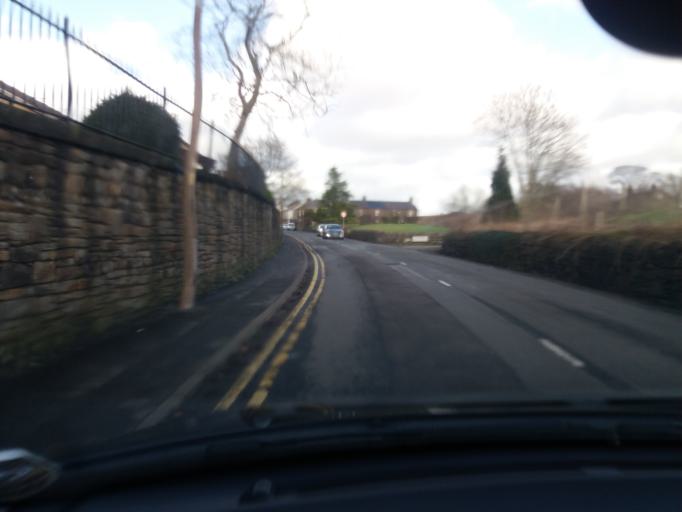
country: GB
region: England
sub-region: Lancashire
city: Adlington
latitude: 53.6209
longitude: -2.5924
